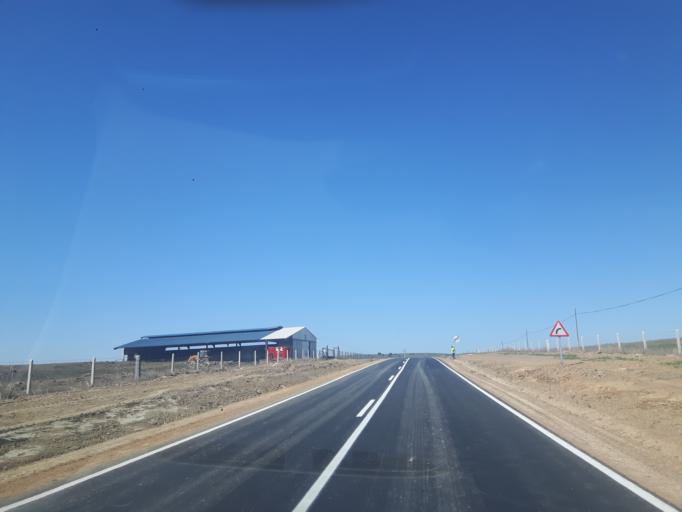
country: ES
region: Castille and Leon
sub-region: Provincia de Salamanca
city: Terradillos
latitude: 40.8241
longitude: -5.5380
